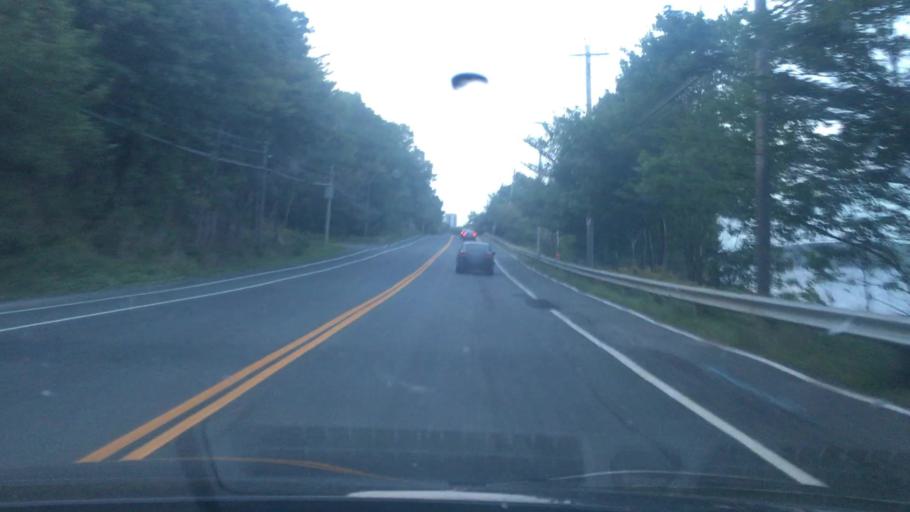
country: CA
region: Nova Scotia
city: Dartmouth
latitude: 44.6888
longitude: -63.6593
